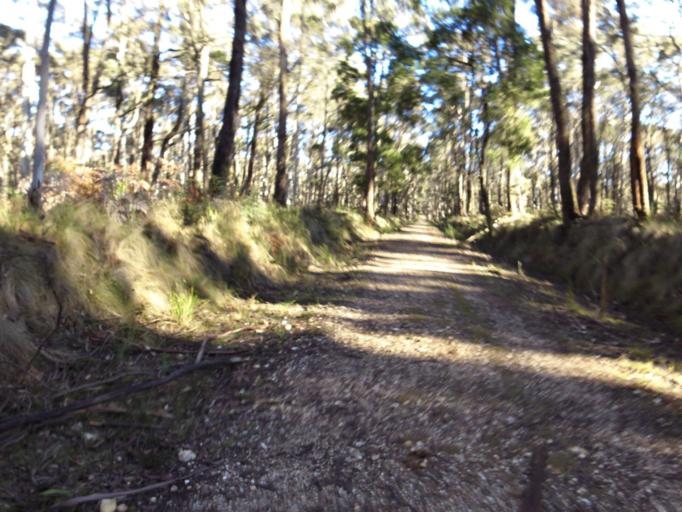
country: AU
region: Victoria
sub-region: Moorabool
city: Bacchus Marsh
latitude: -37.3917
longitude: 144.2856
